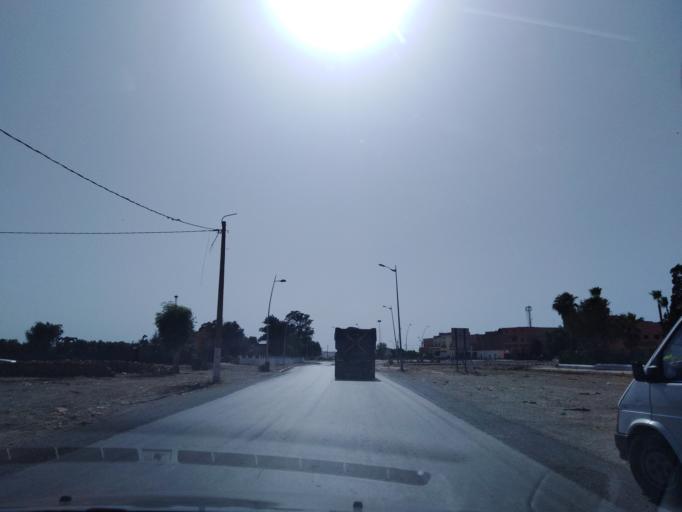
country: MA
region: Doukkala-Abda
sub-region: Safi
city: Safi
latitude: 32.2536
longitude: -8.9808
